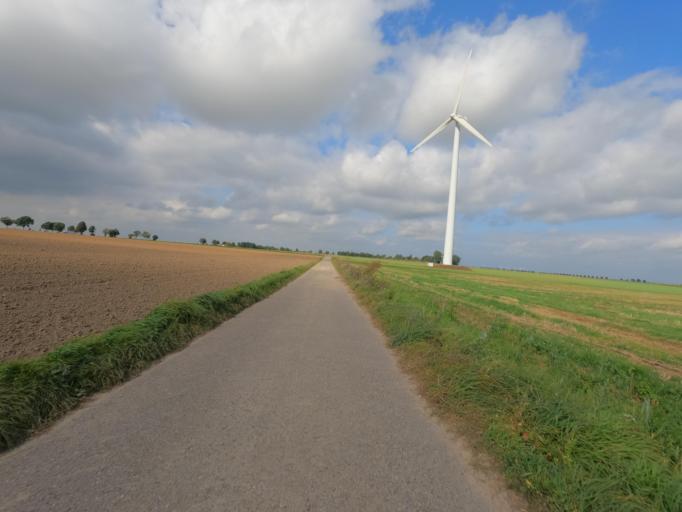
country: DE
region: North Rhine-Westphalia
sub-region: Regierungsbezirk Koln
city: Ubach-Palenberg
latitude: 50.9338
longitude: 6.1394
